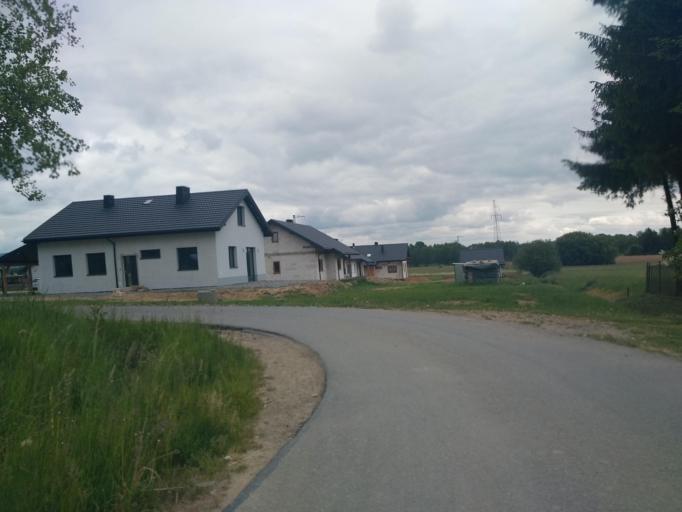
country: PL
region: Subcarpathian Voivodeship
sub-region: Powiat krosnienski
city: Jedlicze
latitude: 49.7204
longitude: 21.6927
